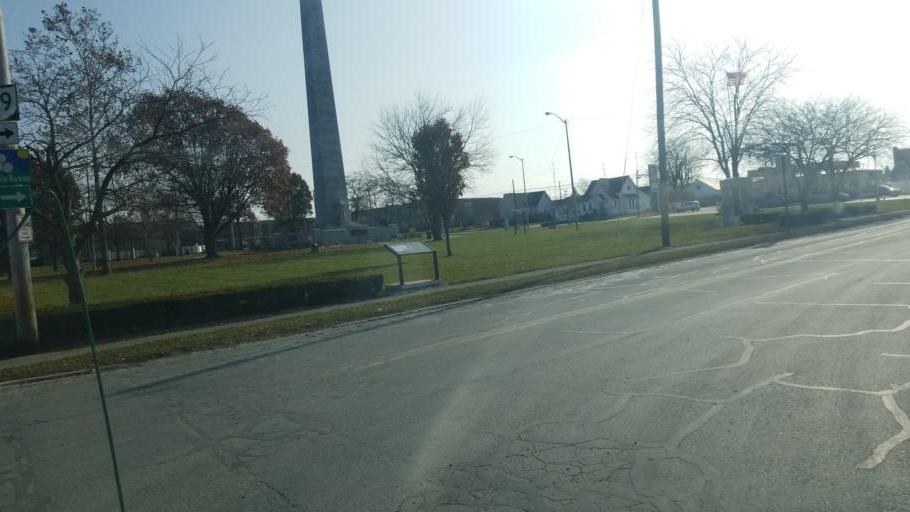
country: US
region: Ohio
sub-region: Mercer County
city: Fort Recovery
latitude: 40.4137
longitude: -84.7766
